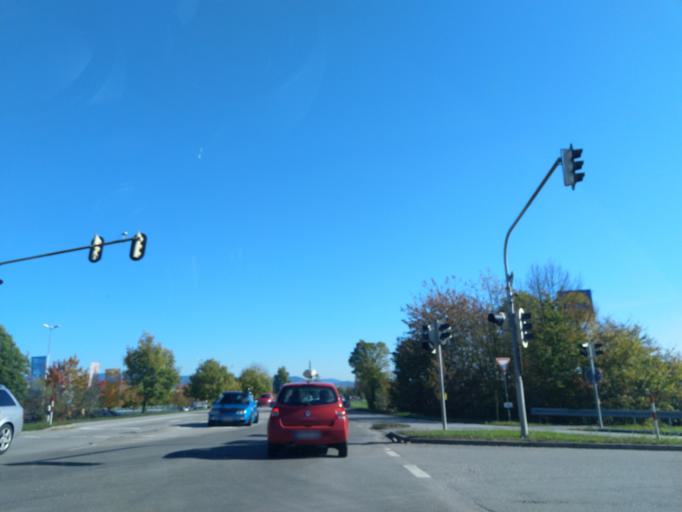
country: DE
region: Bavaria
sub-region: Lower Bavaria
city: Plattling
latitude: 48.7872
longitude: 12.8942
